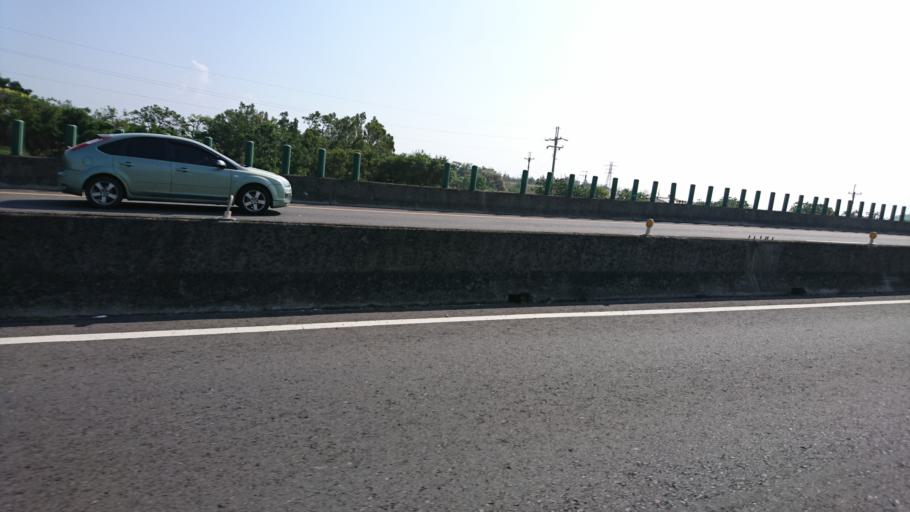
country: TW
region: Taiwan
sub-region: Miaoli
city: Miaoli
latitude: 24.6726
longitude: 120.8380
